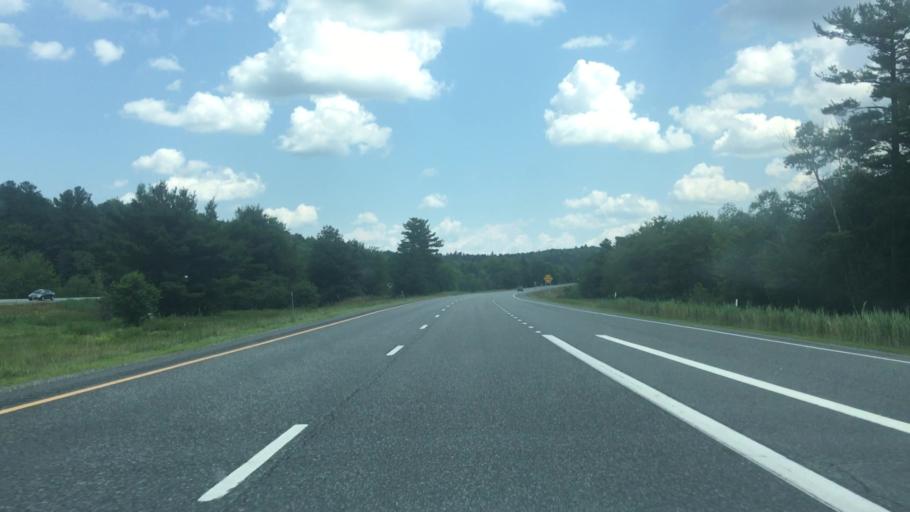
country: US
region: New Hampshire
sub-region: Sullivan County
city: Sunapee
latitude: 43.4406
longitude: -72.0595
